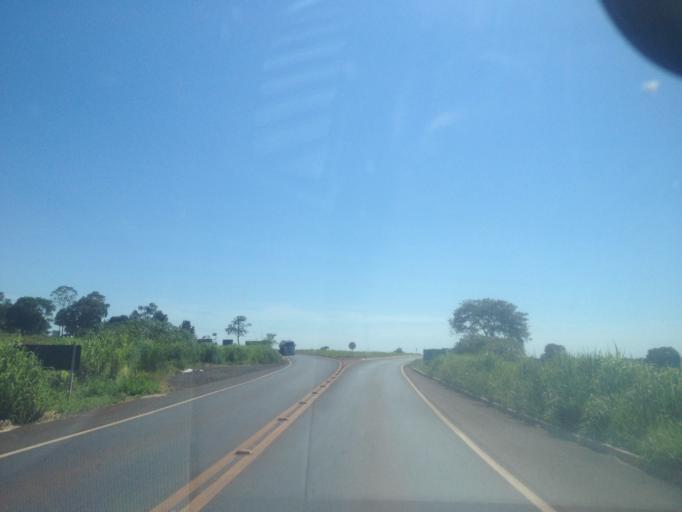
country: BR
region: Minas Gerais
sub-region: Santa Vitoria
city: Santa Vitoria
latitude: -18.8771
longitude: -50.1248
